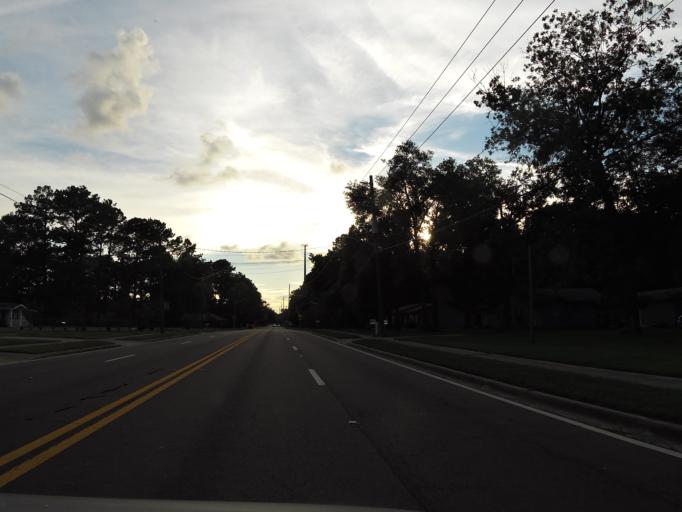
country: US
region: Florida
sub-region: Duval County
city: Jacksonville
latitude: 30.4044
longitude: -81.7106
